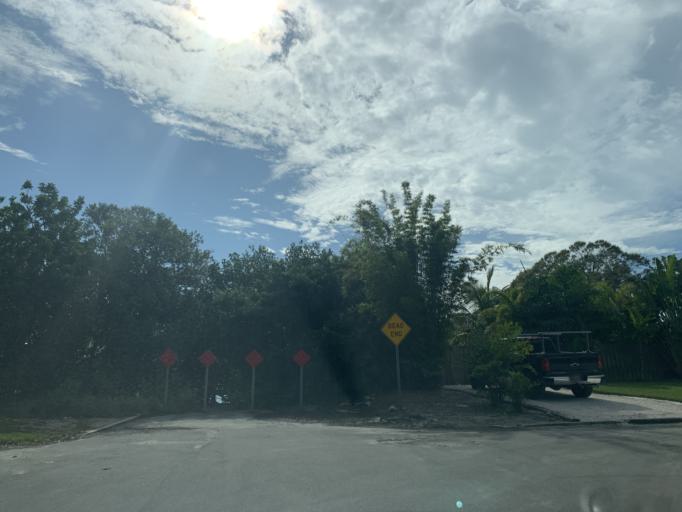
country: US
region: Florida
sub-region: Pinellas County
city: Gulfport
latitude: 27.7430
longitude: -82.6931
